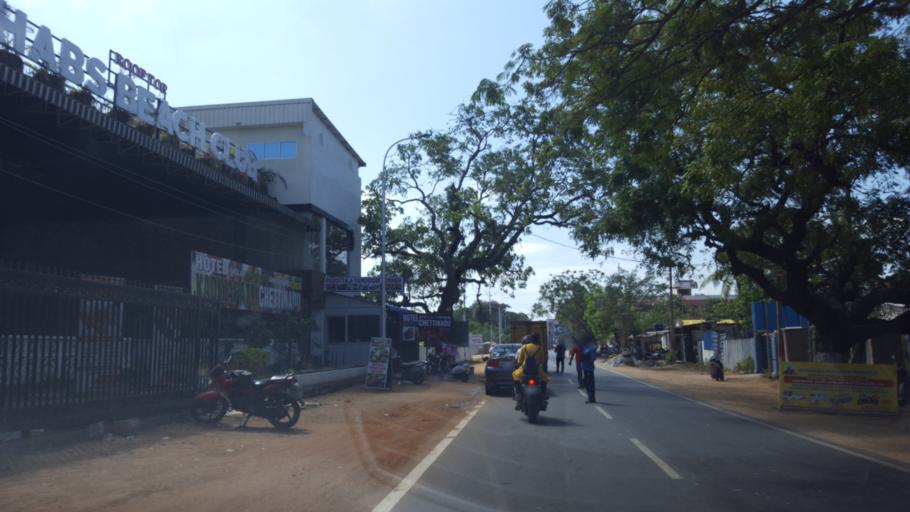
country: IN
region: Tamil Nadu
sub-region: Kancheepuram
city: Mamallapuram
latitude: 12.6265
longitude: 80.1943
